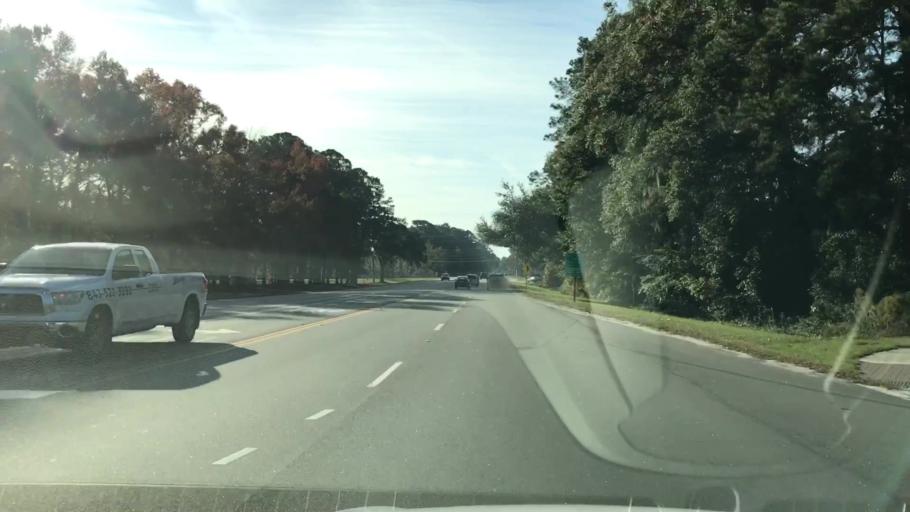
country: US
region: South Carolina
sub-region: Beaufort County
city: Burton
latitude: 32.4575
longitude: -80.7336
